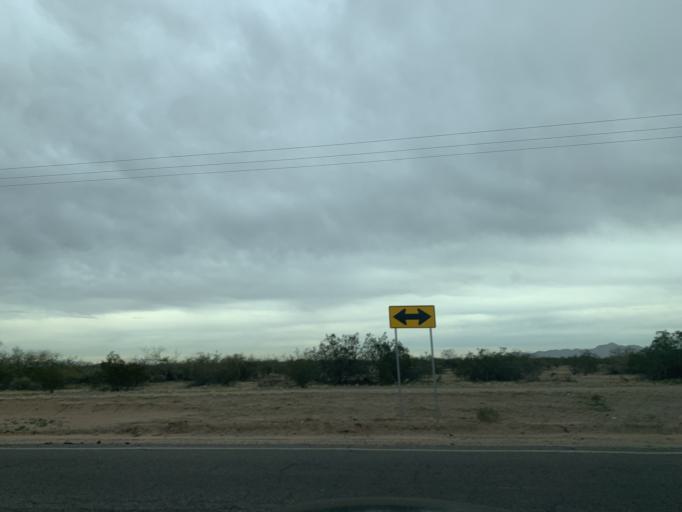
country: US
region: Arizona
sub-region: Pinal County
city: Arizona City
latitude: 32.8031
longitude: -111.6711
